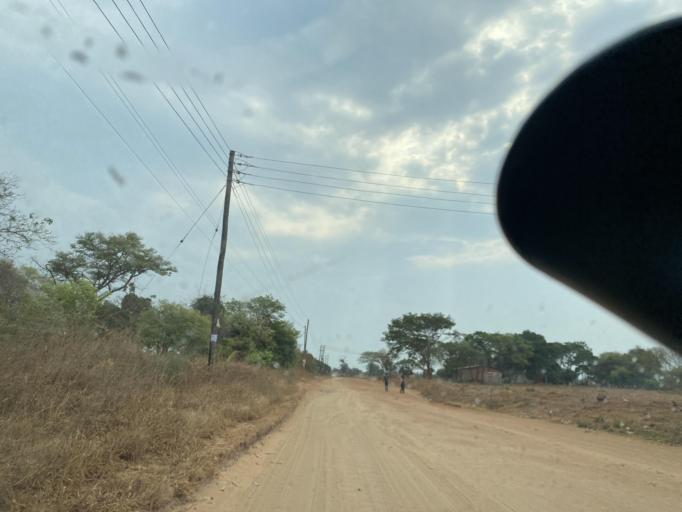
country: ZM
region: Lusaka
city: Lusaka
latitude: -15.2900
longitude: 28.2793
